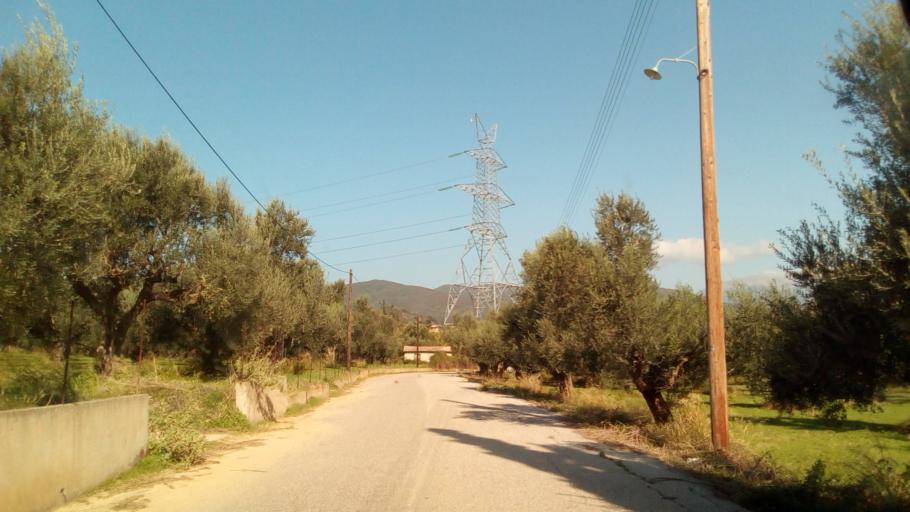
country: GR
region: West Greece
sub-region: Nomos Aitolias kai Akarnanias
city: Antirrio
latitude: 38.3438
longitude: 21.7615
